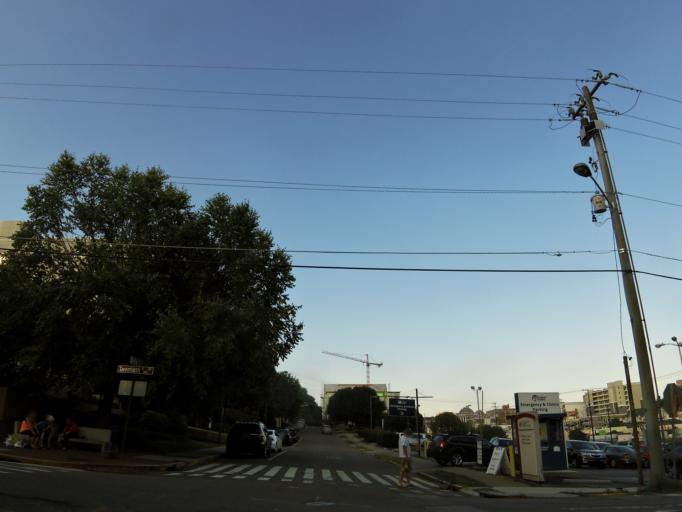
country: US
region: Tennessee
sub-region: Knox County
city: Knoxville
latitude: 35.9558
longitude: -83.9373
